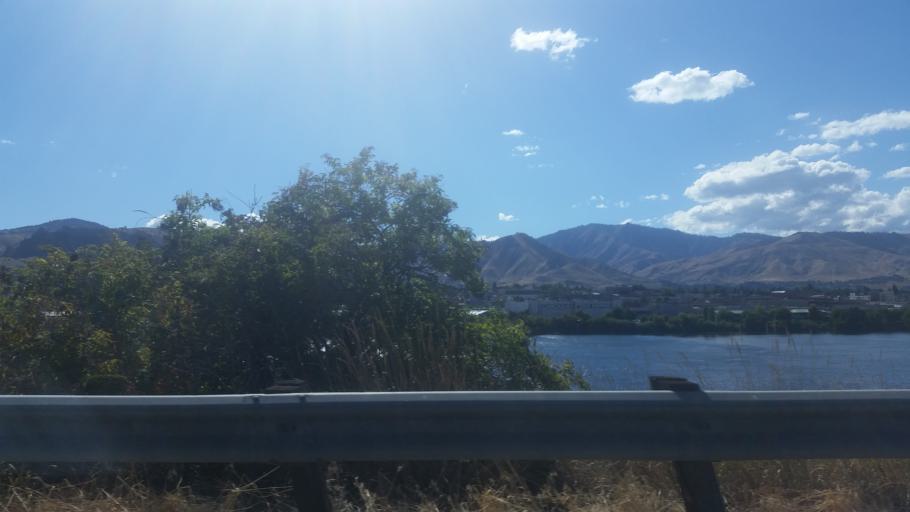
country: US
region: Washington
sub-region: Douglas County
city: East Wenatchee
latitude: 47.4219
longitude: -120.2973
